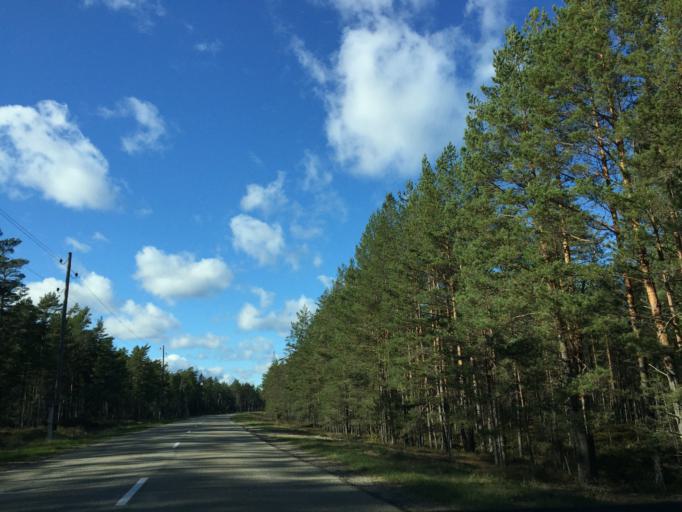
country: LV
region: Mesraga
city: Mersrags
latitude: 57.3993
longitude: 22.9724
